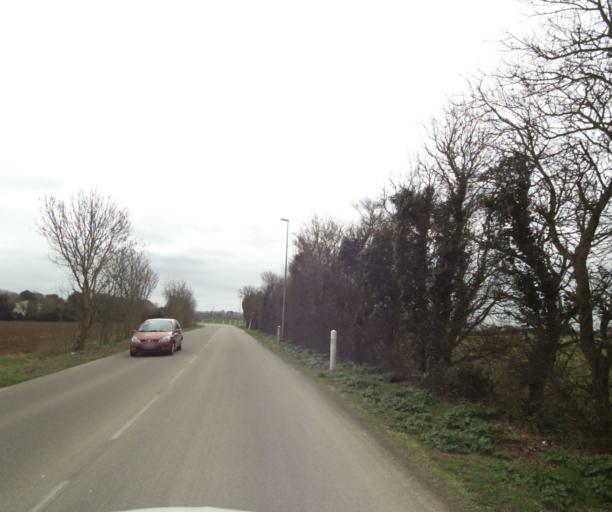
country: FR
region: Poitou-Charentes
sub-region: Departement de la Charente-Maritime
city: Nieul-sur-Mer
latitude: 46.1876
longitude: -1.1810
